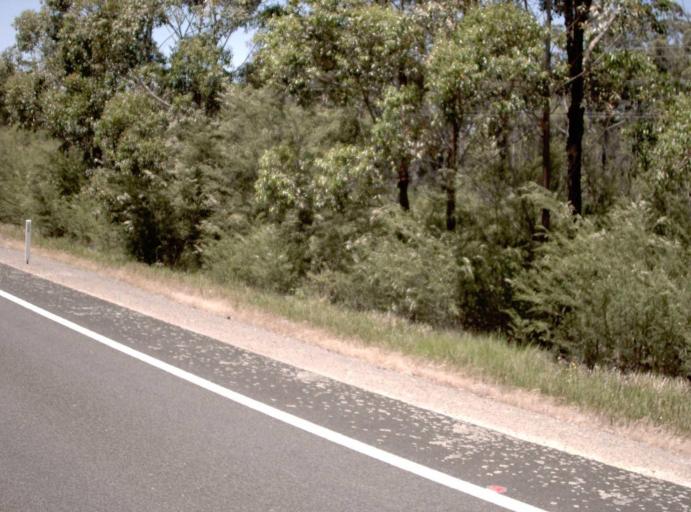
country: AU
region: Victoria
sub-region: East Gippsland
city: Lakes Entrance
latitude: -37.7507
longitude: 148.3634
